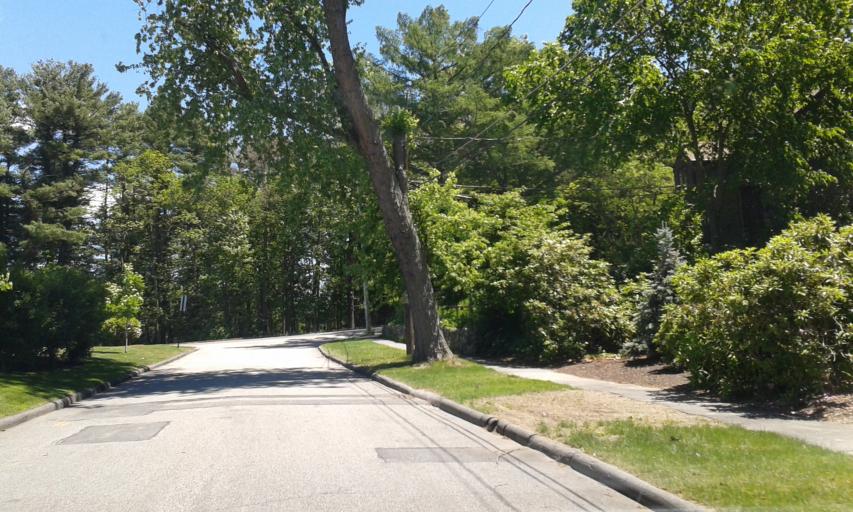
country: US
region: Massachusetts
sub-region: Middlesex County
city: Winchester
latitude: 42.4639
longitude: -71.1214
